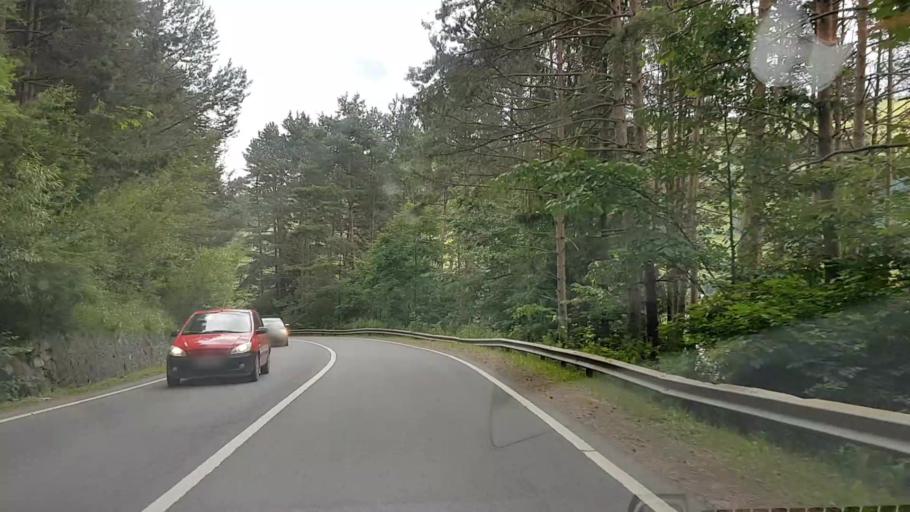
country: RO
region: Neamt
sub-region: Comuna Borca
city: Borca
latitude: 47.1724
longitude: 25.7941
